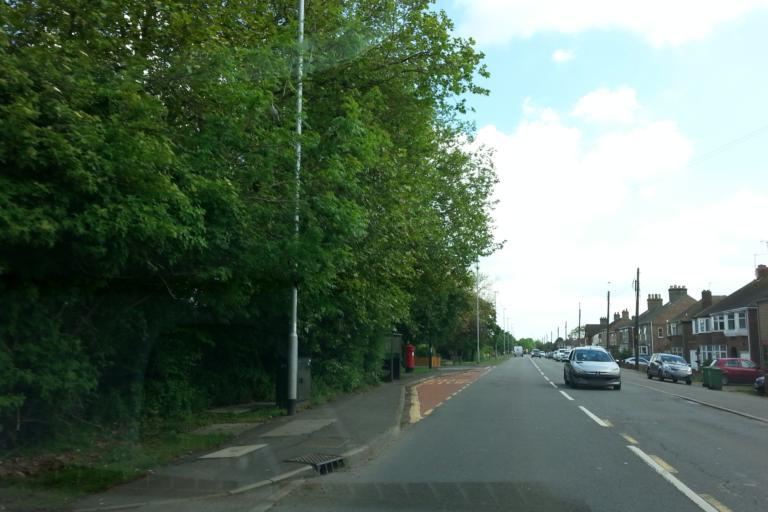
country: GB
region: England
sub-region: Cambridgeshire
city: Yaxley
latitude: 52.5164
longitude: -0.2632
